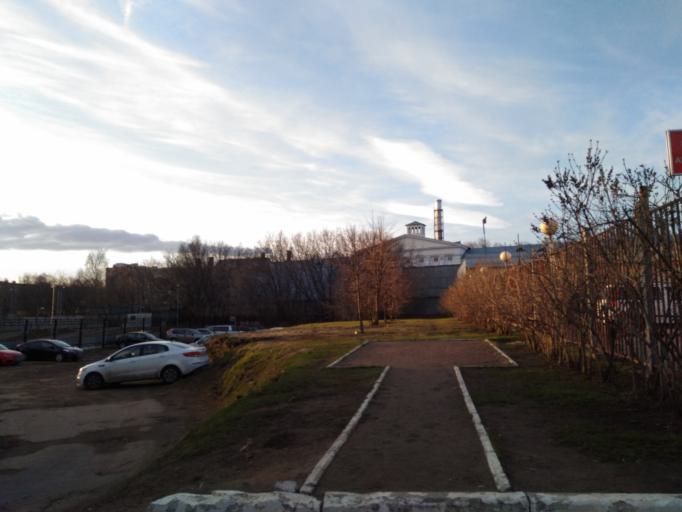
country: RU
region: Moskovskaya
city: Khoroshevo-Mnevniki
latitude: 55.7901
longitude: 37.4602
